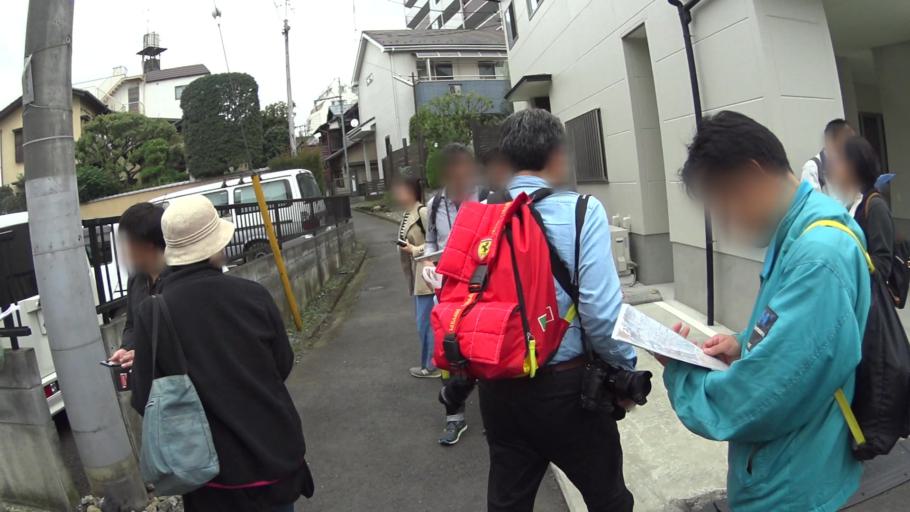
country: JP
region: Saitama
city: Hanno
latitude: 35.8534
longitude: 139.3164
